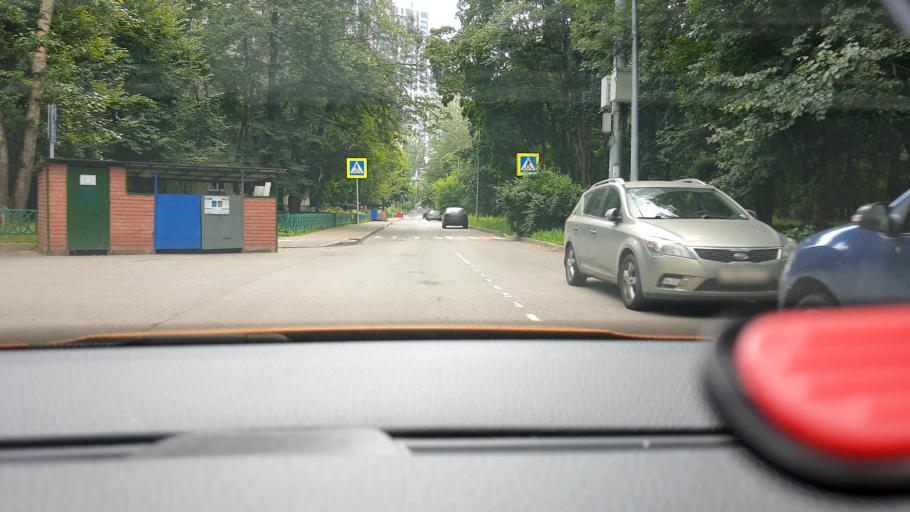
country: RU
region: Moskovskaya
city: Levoberezhnyy
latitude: 55.8613
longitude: 37.4750
